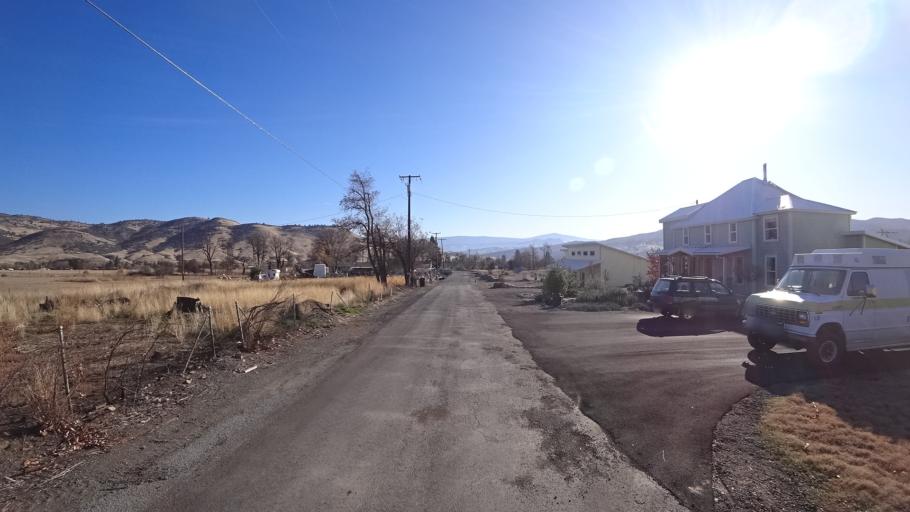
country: US
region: California
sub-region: Siskiyou County
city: Montague
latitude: 41.9026
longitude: -122.5649
